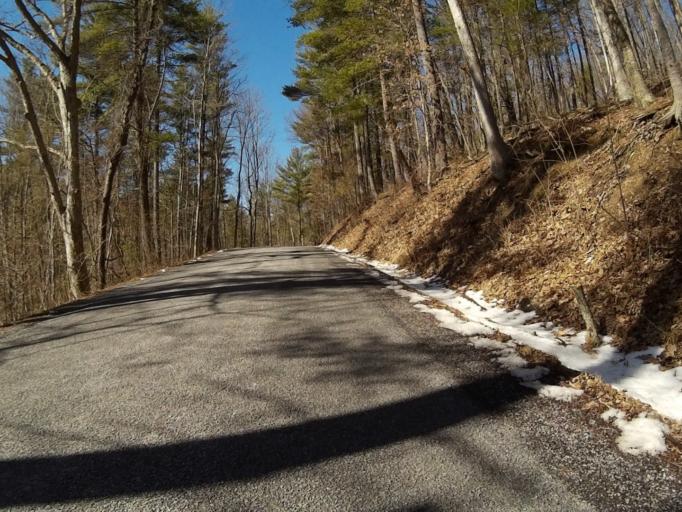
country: US
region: Pennsylvania
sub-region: Centre County
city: Stormstown
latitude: 40.8402
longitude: -78.0242
